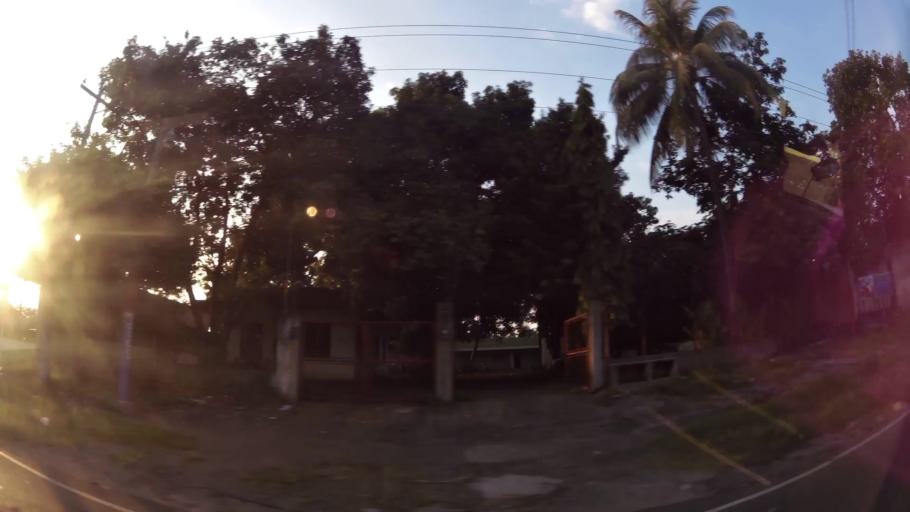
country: GT
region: Retalhuleu
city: San Sebastian
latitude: 14.5571
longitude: -91.6537
